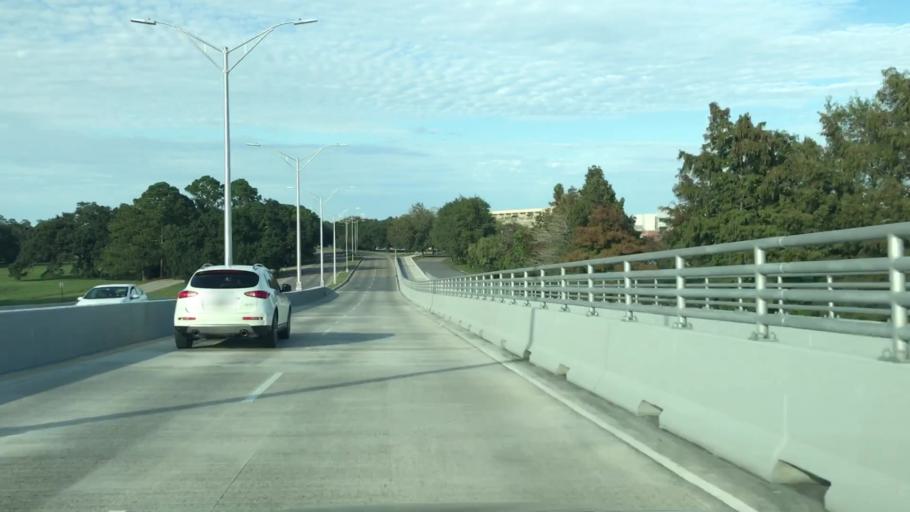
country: US
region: Louisiana
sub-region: Orleans Parish
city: New Orleans
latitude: 29.9941
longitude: -90.0865
